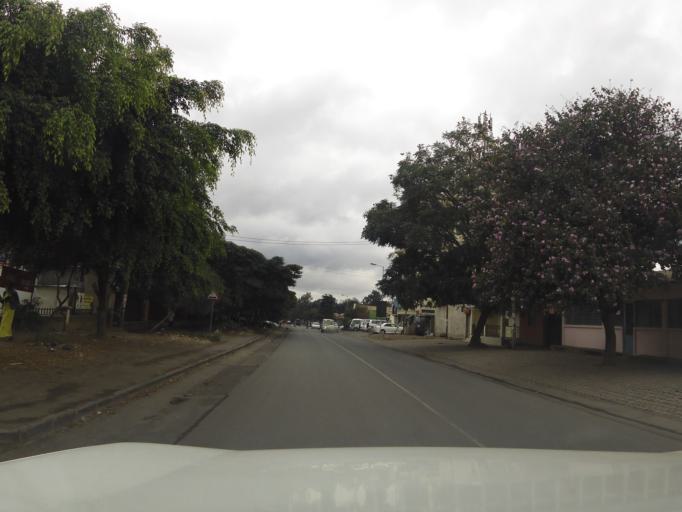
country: TZ
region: Arusha
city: Arusha
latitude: -3.3656
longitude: 36.6834
